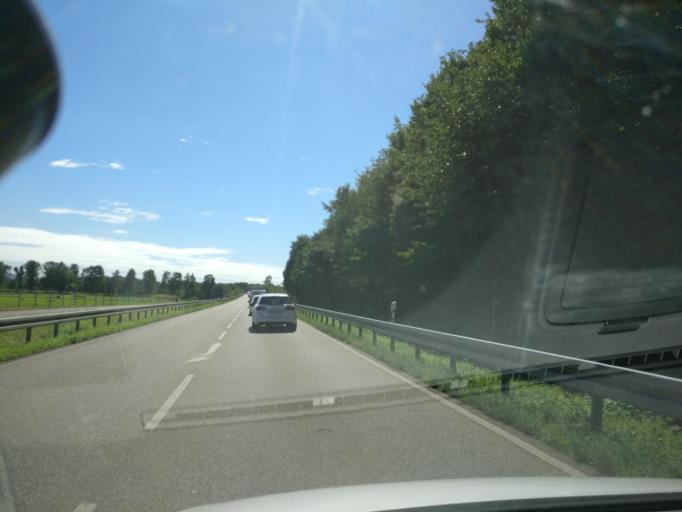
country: DE
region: Baden-Wuerttemberg
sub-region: Karlsruhe Region
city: Karlsruhe
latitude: 48.9866
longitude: 8.4435
